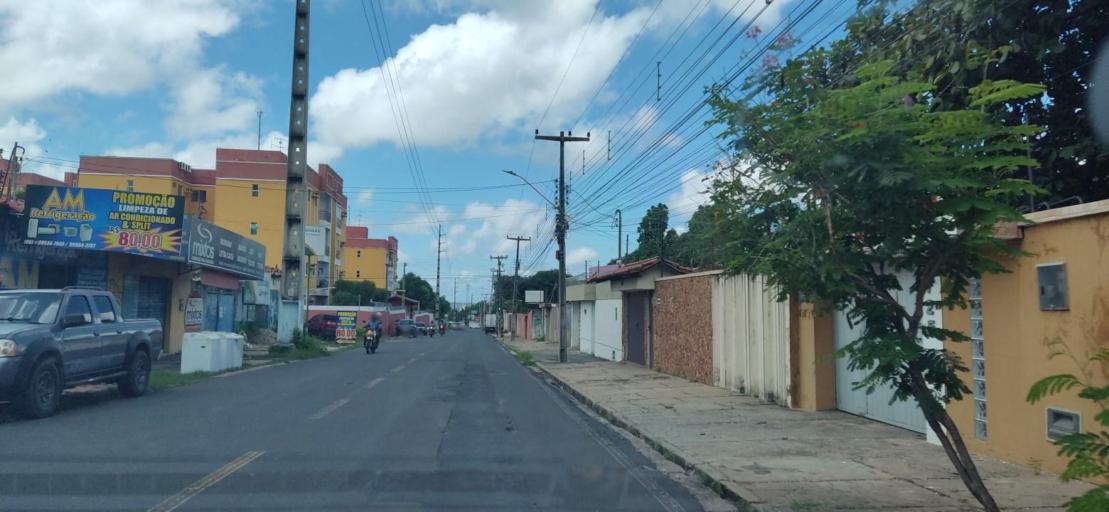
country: BR
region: Piaui
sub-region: Teresina
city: Teresina
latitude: -5.0673
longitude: -42.7601
